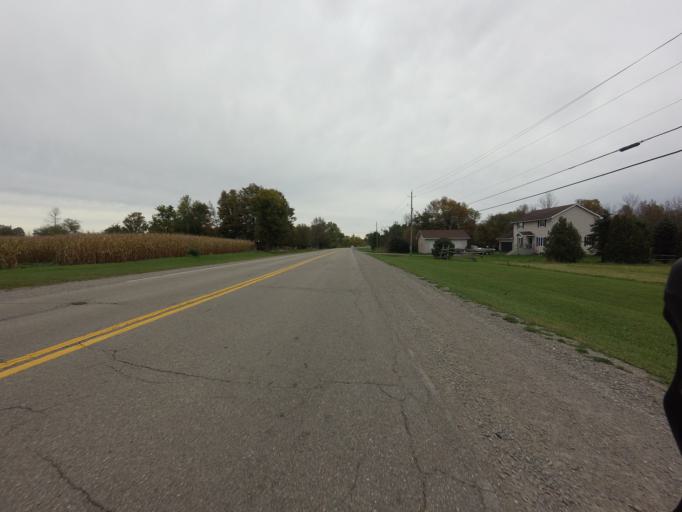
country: CA
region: Ontario
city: Brockville
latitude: 44.6502
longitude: -75.9016
